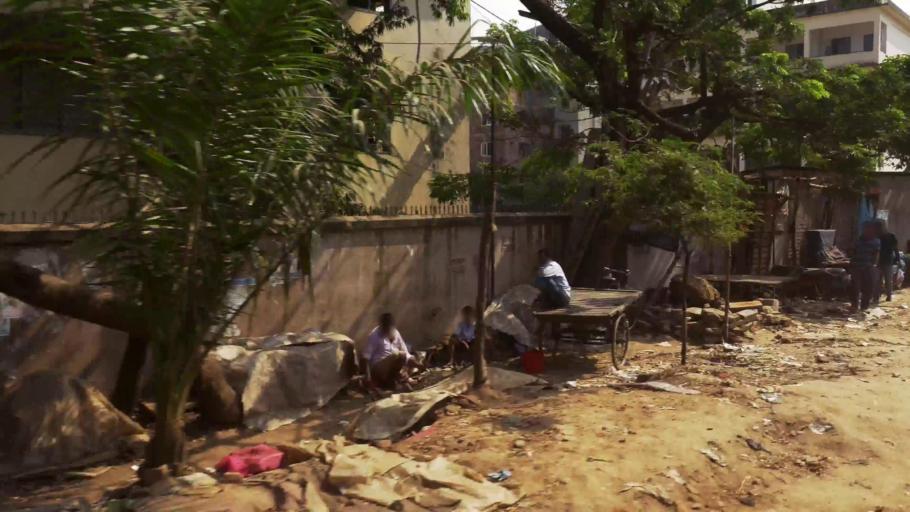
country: BD
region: Dhaka
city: Paltan
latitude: 23.8040
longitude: 90.4020
